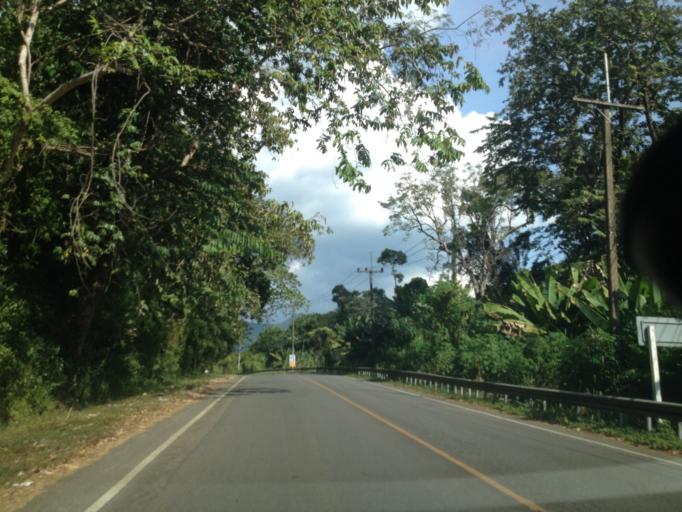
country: TH
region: Chiang Mai
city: Samoeng
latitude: 18.8486
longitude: 98.7377
